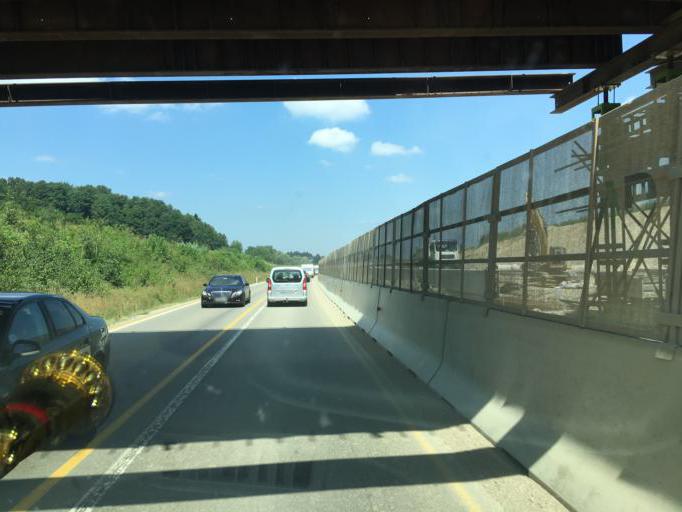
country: SI
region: Podlehnik
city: Podlehnik
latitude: 46.3489
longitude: 15.8690
